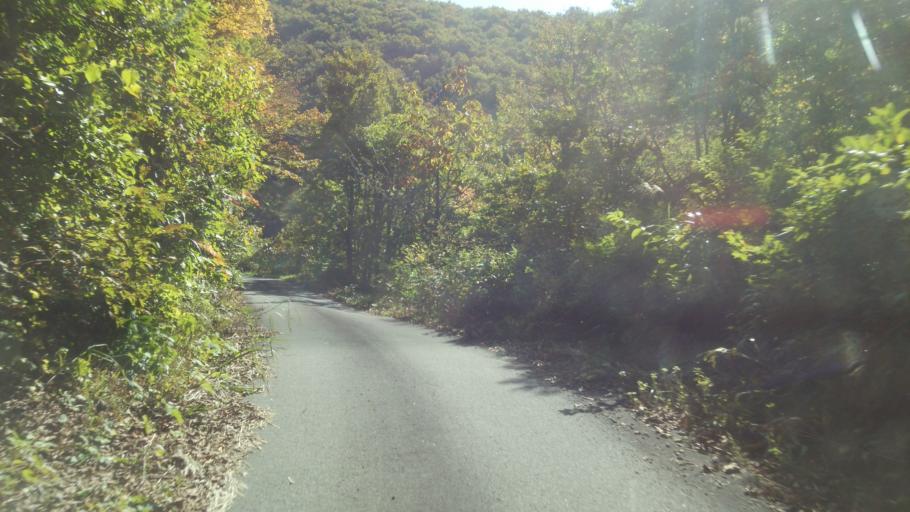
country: JP
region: Fukushima
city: Kitakata
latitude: 37.6202
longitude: 139.9890
